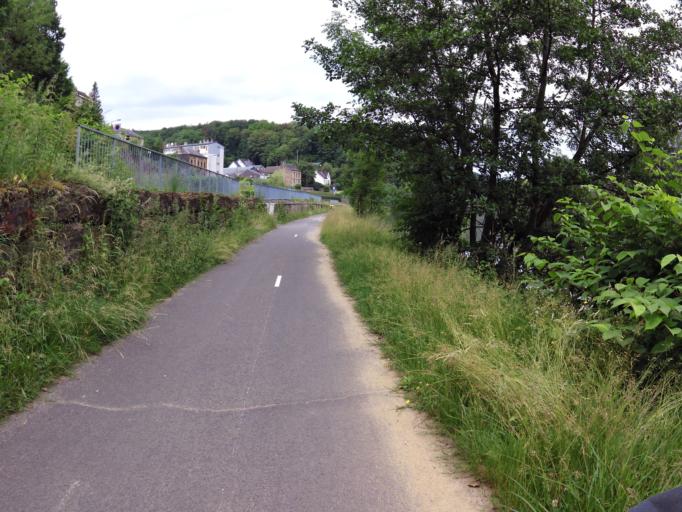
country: FR
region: Champagne-Ardenne
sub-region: Departement des Ardennes
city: Nouzonville
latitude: 49.8115
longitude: 4.7401
